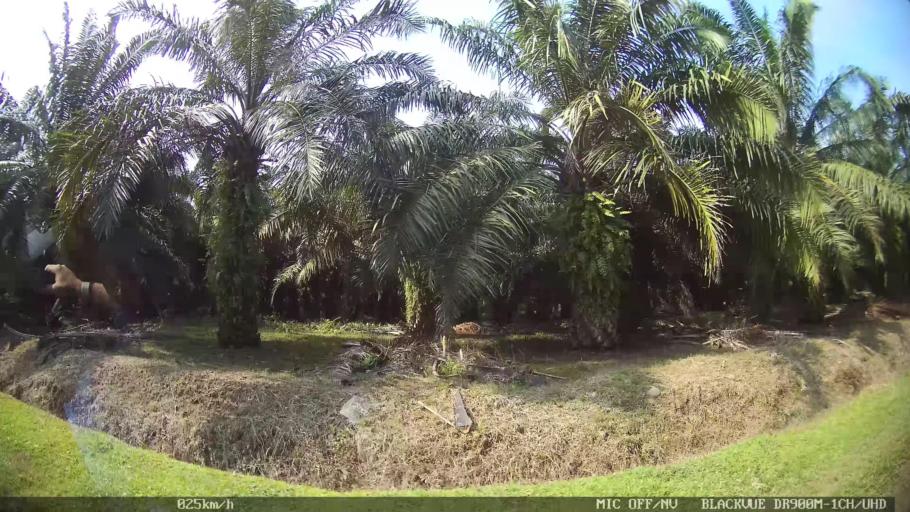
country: ID
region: North Sumatra
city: Binjai
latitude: 3.6428
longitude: 98.5231
